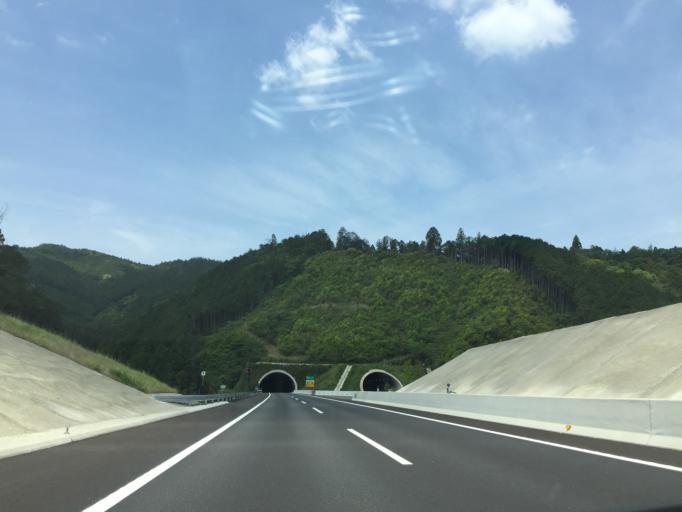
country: JP
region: Aichi
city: Shinshiro
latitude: 34.9113
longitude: 137.6031
